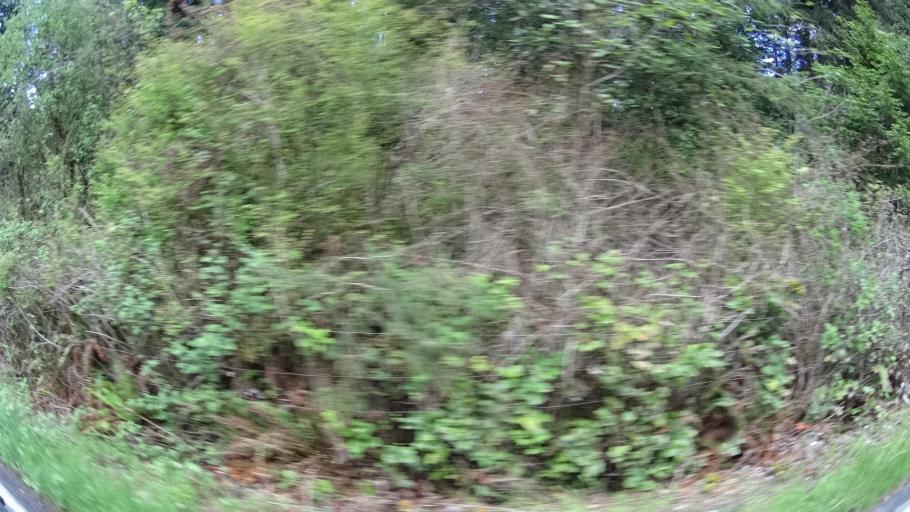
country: US
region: California
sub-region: Humboldt County
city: Blue Lake
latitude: 40.9133
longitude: -124.0232
